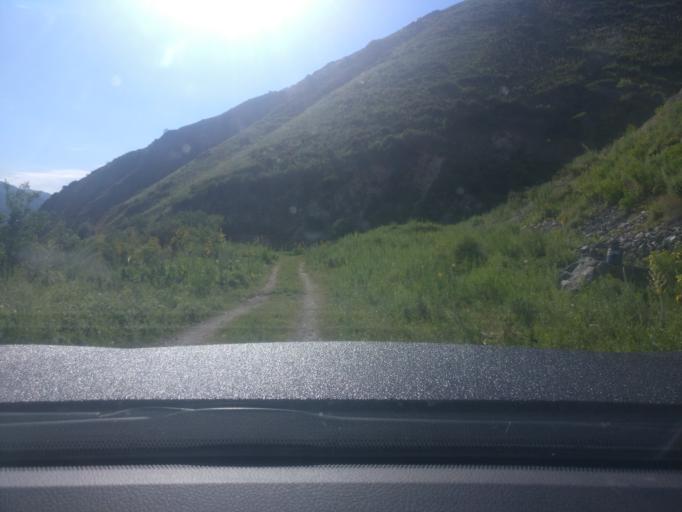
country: KZ
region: Almaty Qalasy
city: Almaty
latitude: 43.1077
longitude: 76.9542
